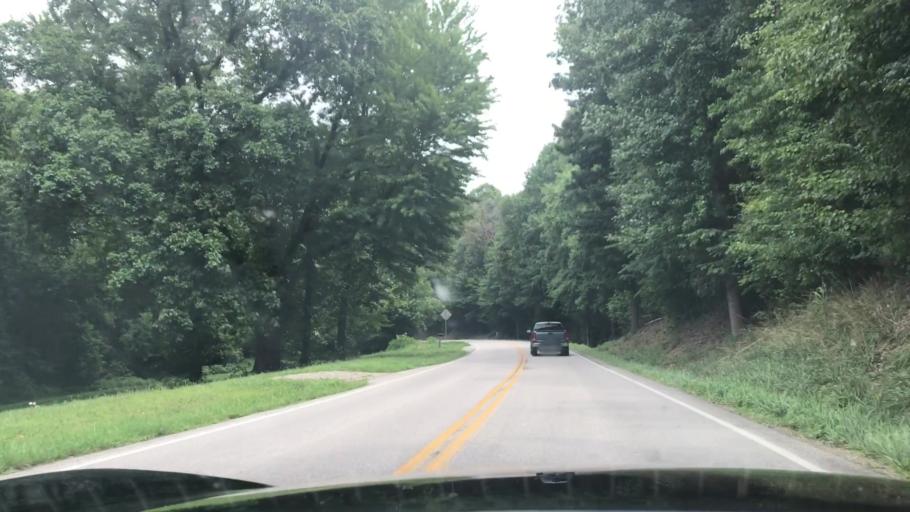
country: US
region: Kentucky
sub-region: Butler County
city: Morgantown
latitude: 37.2075
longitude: -86.7252
